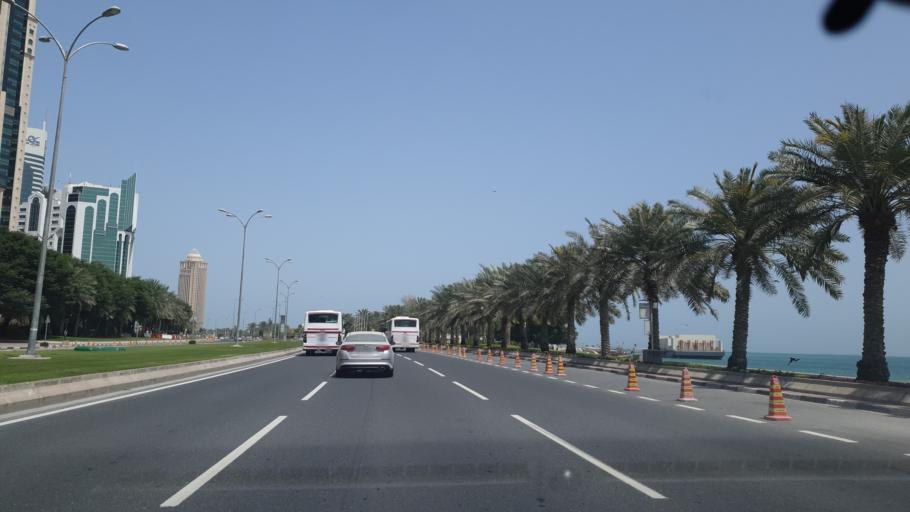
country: QA
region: Baladiyat ad Dawhah
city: Doha
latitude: 25.3160
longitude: 51.5274
